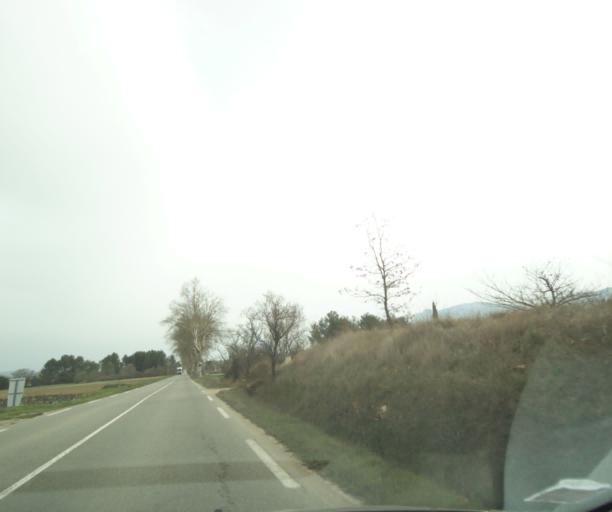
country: FR
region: Provence-Alpes-Cote d'Azur
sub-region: Departement des Bouches-du-Rhone
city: Trets
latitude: 43.4539
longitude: 5.6998
